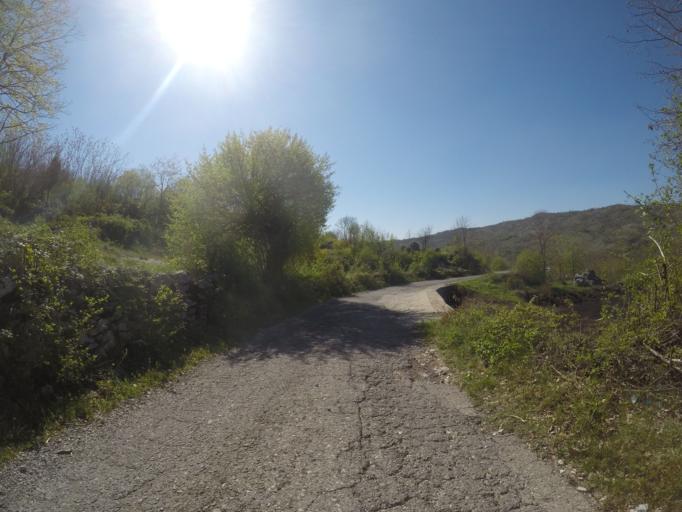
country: ME
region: Danilovgrad
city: Danilovgrad
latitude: 42.5233
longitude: 19.0495
